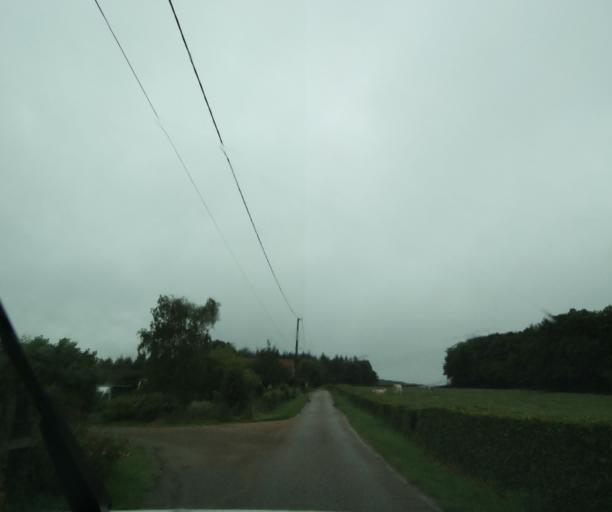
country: FR
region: Bourgogne
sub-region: Departement de Saone-et-Loire
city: Charolles
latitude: 46.3928
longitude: 4.3148
